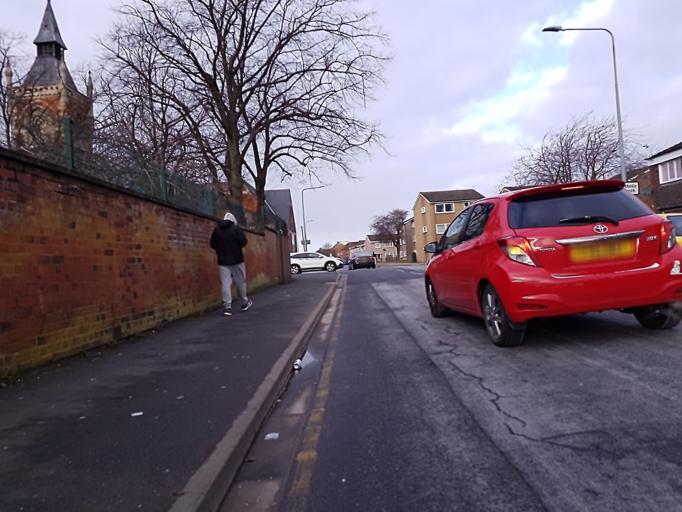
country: GB
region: England
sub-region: North East Lincolnshire
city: Grimsby
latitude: 53.5684
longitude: -0.0706
